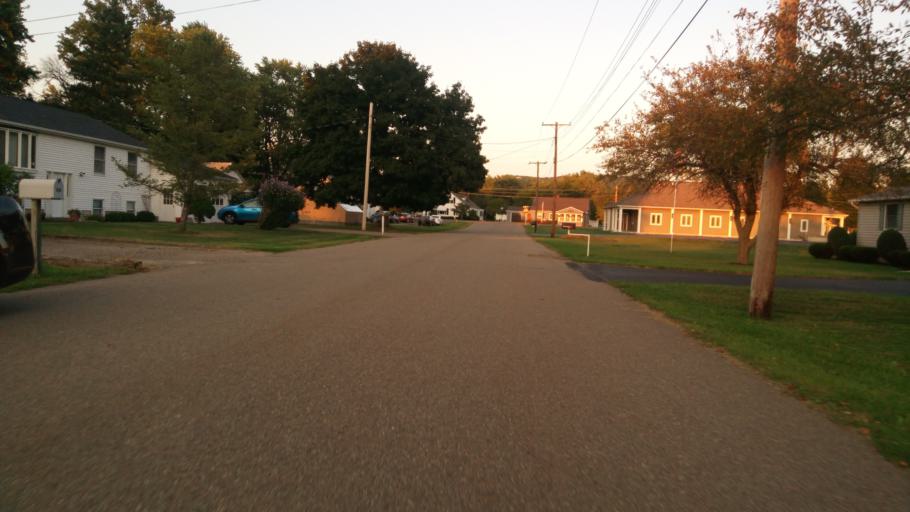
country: US
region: New York
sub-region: Chemung County
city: Elmira
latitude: 42.0658
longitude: -76.7872
